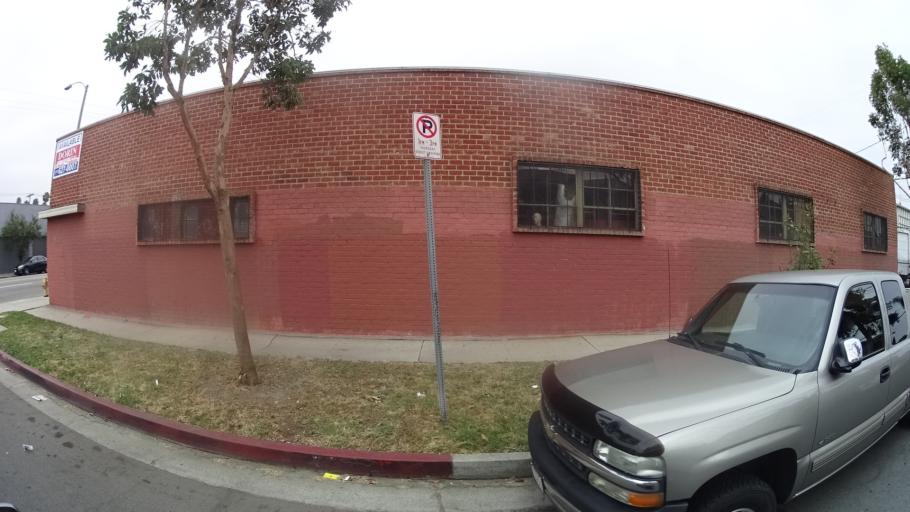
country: US
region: California
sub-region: Los Angeles County
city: View Park-Windsor Hills
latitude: 34.0258
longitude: -118.3395
